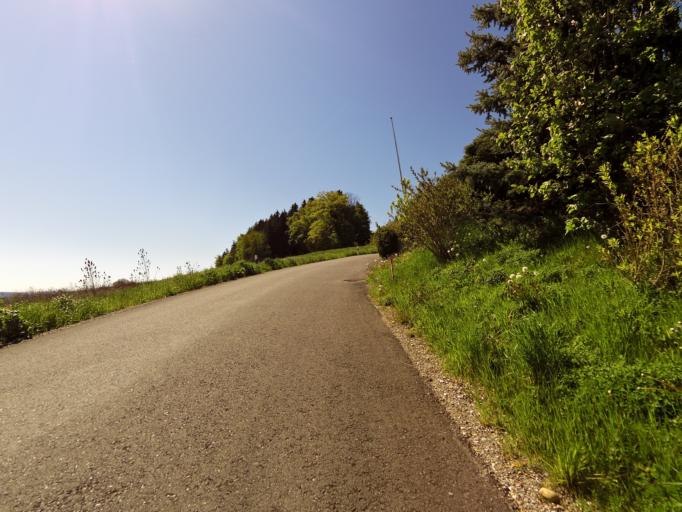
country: CH
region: Thurgau
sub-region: Weinfelden District
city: Berg
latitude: 47.5817
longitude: 9.1585
